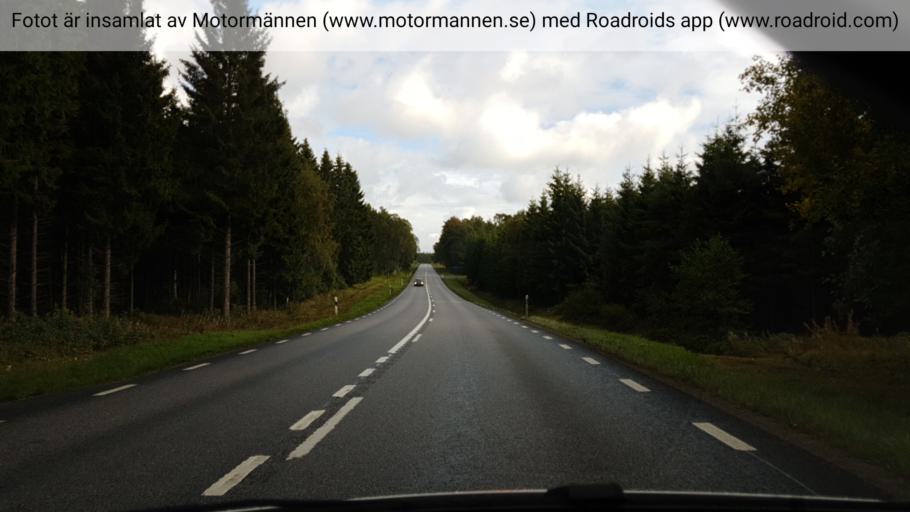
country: SE
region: Joenkoeping
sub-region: Mullsjo Kommun
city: Mullsjoe
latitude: 58.0499
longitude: 13.8075
